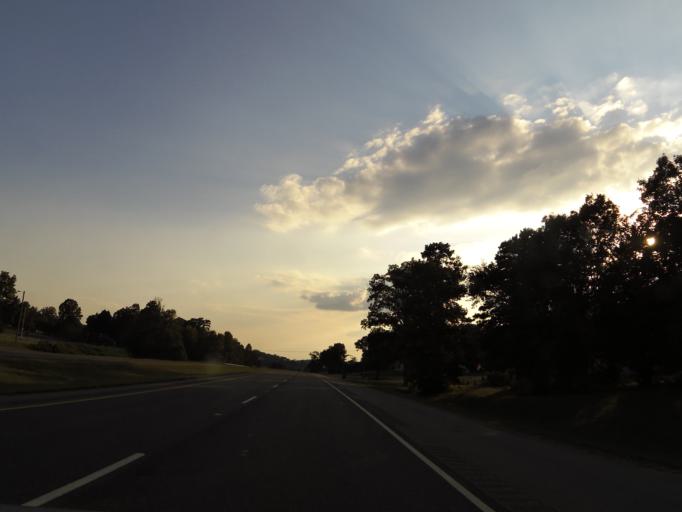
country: US
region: Tennessee
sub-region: Knox County
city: Mascot
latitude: 36.0429
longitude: -83.8259
